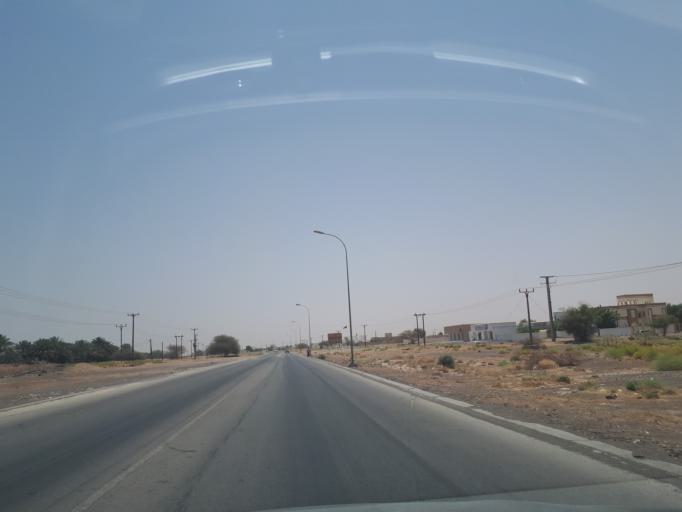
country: OM
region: Ash Sharqiyah
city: Badiyah
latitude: 22.5001
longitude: 58.7508
